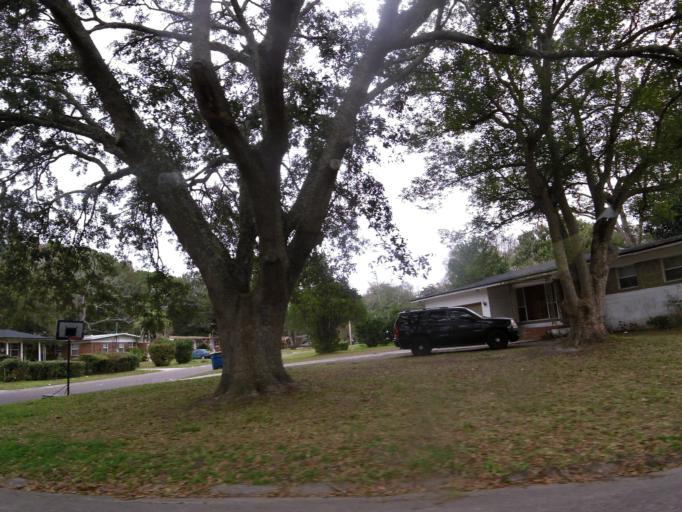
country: US
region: Florida
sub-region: Duval County
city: Jacksonville
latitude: 30.3719
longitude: -81.7103
